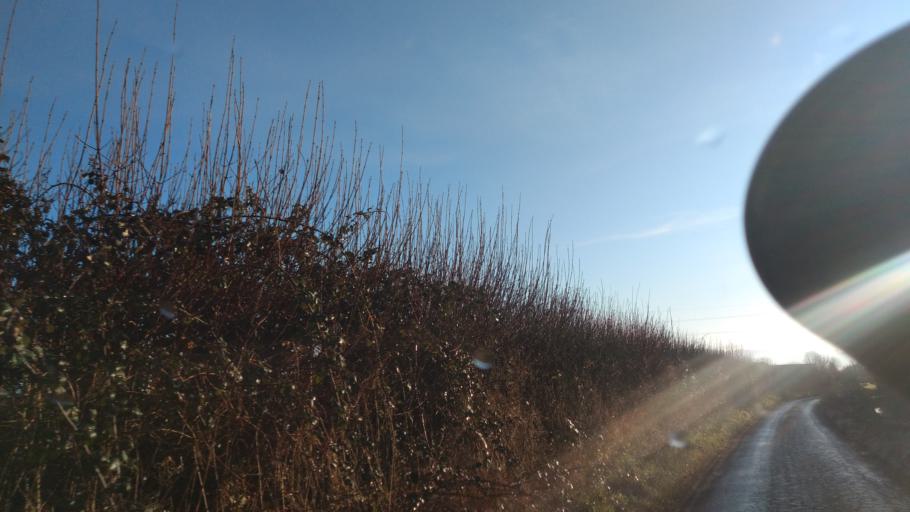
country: GB
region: England
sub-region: Wiltshire
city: Lacock
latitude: 51.4317
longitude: -2.1387
